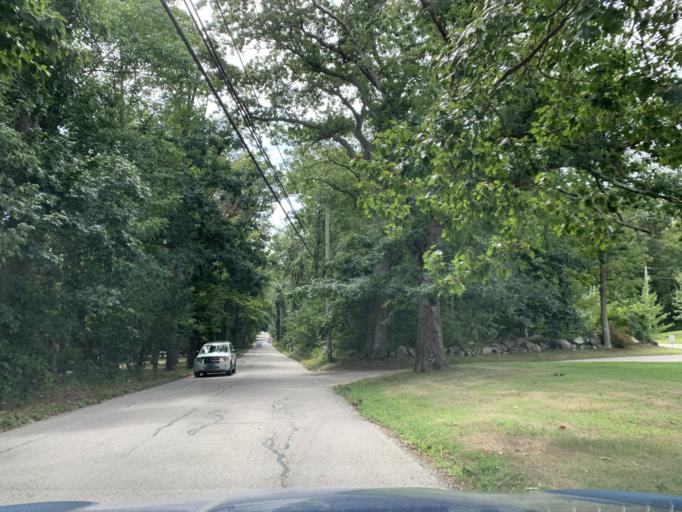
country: US
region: Rhode Island
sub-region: Washington County
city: Exeter
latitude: 41.5568
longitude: -71.6220
